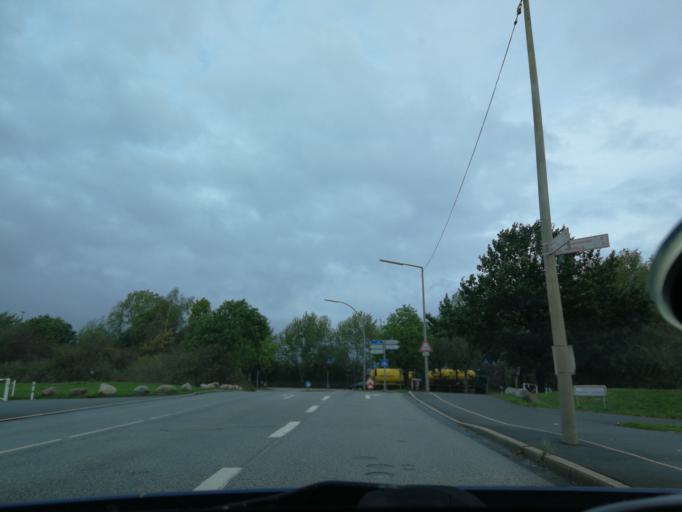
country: DE
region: Hamburg
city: Harburg
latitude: 53.4760
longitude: 9.9375
